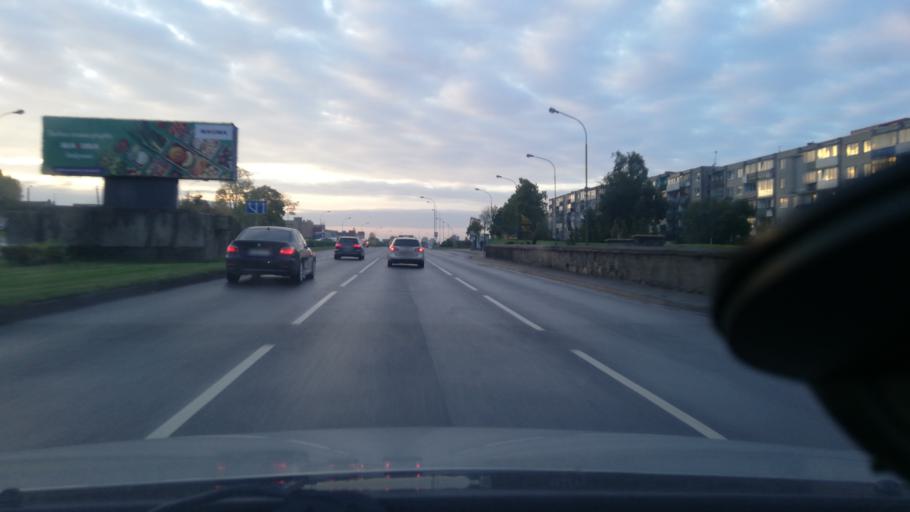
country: LT
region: Klaipedos apskritis
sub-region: Klaipeda
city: Klaipeda
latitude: 55.6890
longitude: 21.1810
